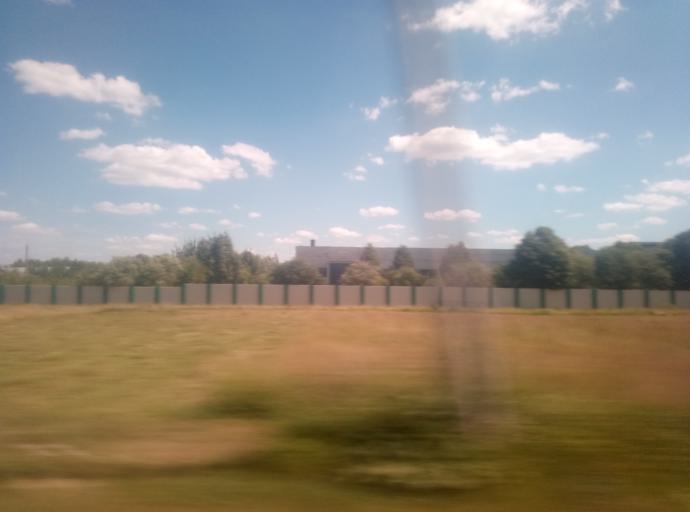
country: RU
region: Tula
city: Kireyevsk
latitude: 53.9600
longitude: 37.9379
